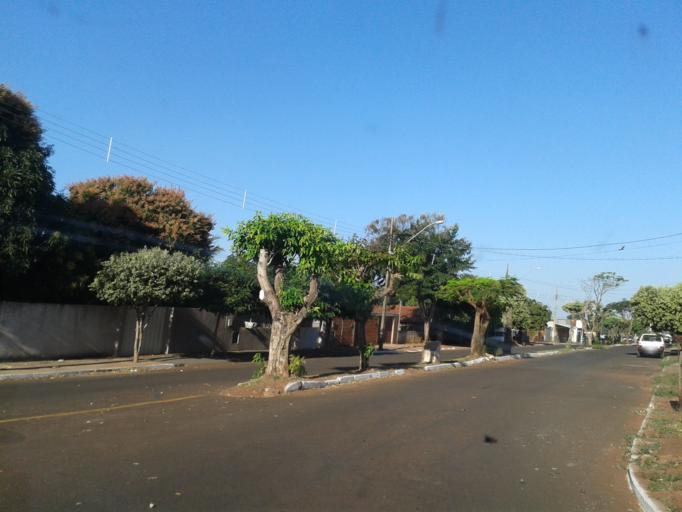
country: BR
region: Minas Gerais
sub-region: Santa Vitoria
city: Santa Vitoria
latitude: -18.8333
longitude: -50.1363
